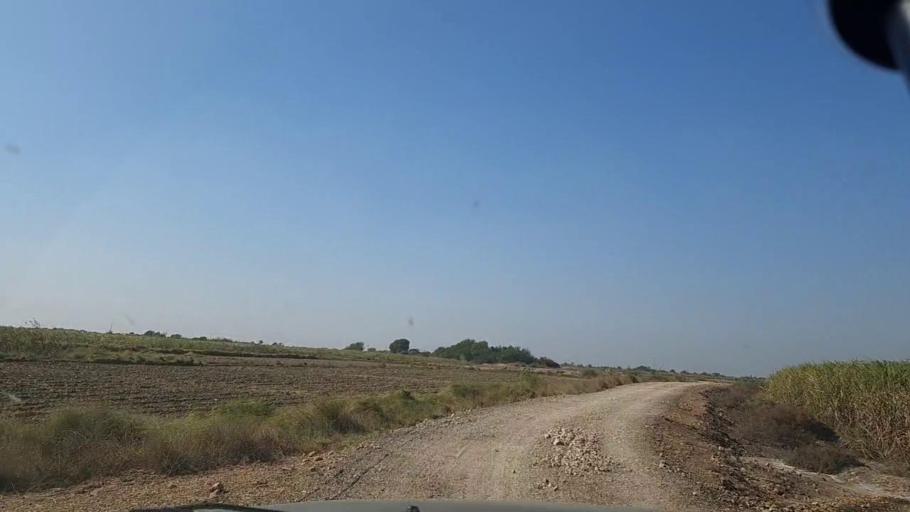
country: PK
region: Sindh
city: Chuhar Jamali
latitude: 24.5753
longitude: 68.0407
